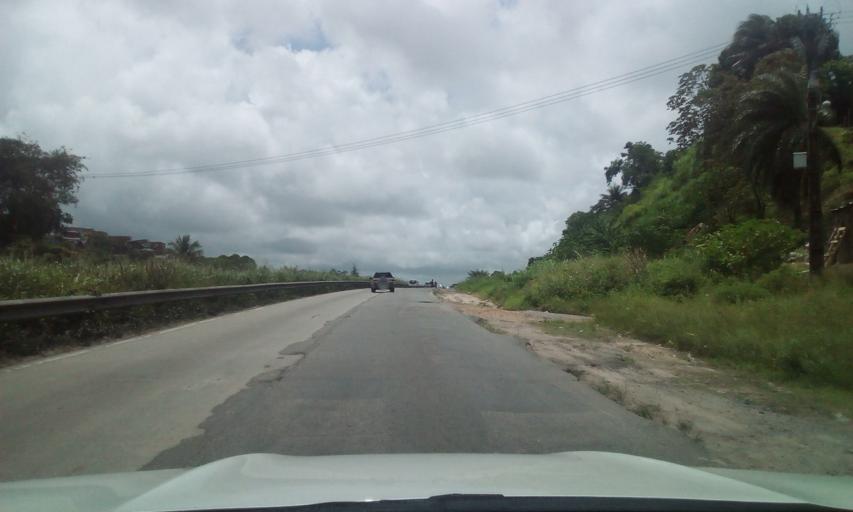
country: BR
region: Pernambuco
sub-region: Jaboatao Dos Guararapes
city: Jaboatao dos Guararapes
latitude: -8.1250
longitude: -34.9438
